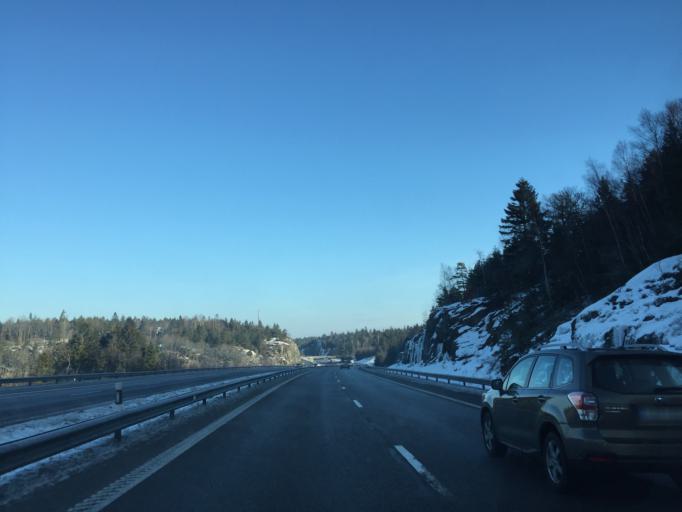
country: SE
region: Vaestra Goetaland
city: Svanesund
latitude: 58.1481
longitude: 11.8846
